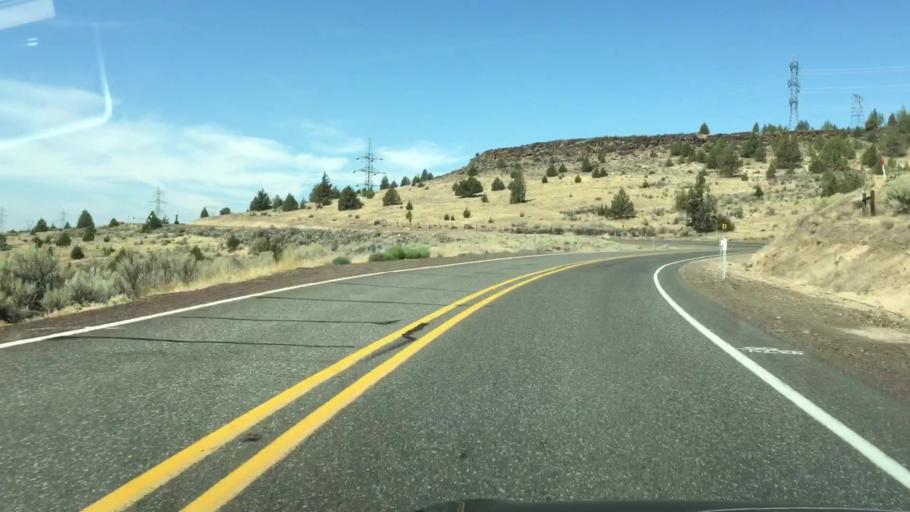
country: US
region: Oregon
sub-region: Wasco County
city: The Dalles
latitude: 45.1691
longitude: -121.0985
